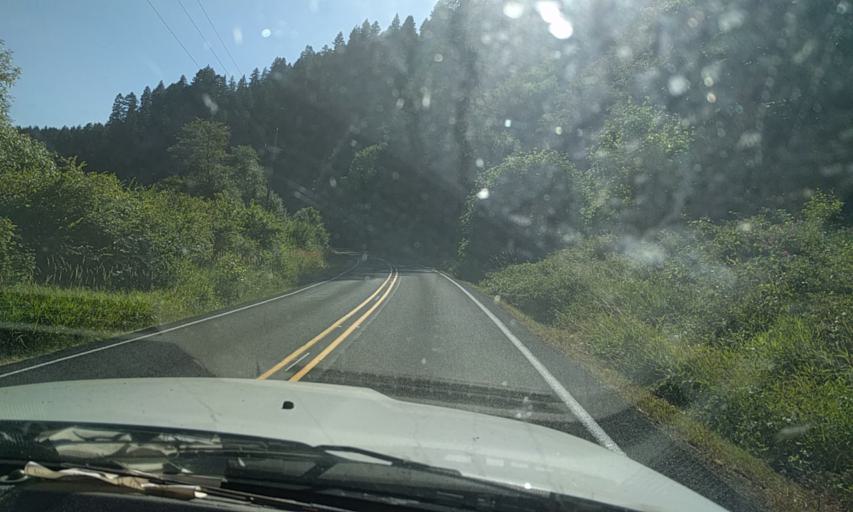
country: US
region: Oregon
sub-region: Lane County
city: Florence
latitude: 44.0765
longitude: -123.8710
